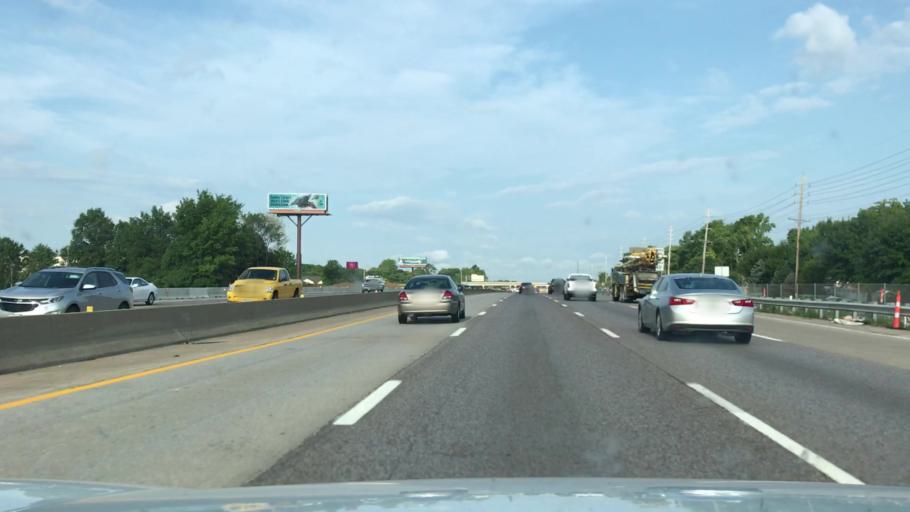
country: US
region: Missouri
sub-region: Saint Charles County
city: O'Fallon
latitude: 38.8026
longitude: -90.6877
